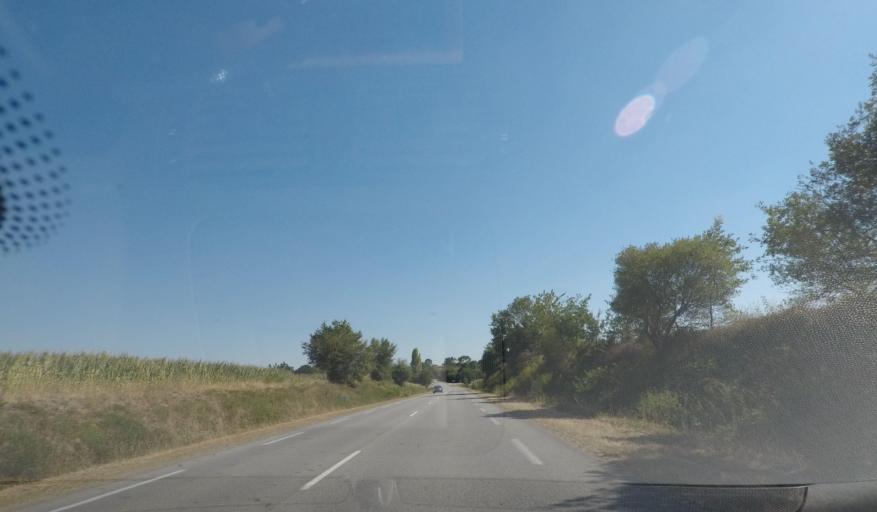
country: FR
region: Brittany
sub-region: Departement du Morbihan
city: Questembert
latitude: 47.6417
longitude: -2.4257
